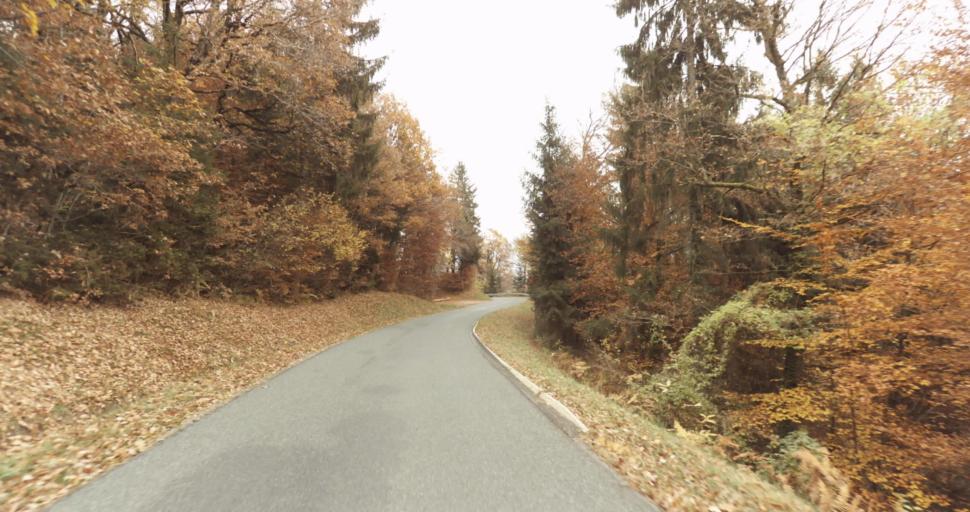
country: FR
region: Rhone-Alpes
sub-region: Departement de la Haute-Savoie
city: Saint-Martin-Bellevue
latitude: 45.9550
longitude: 6.1534
